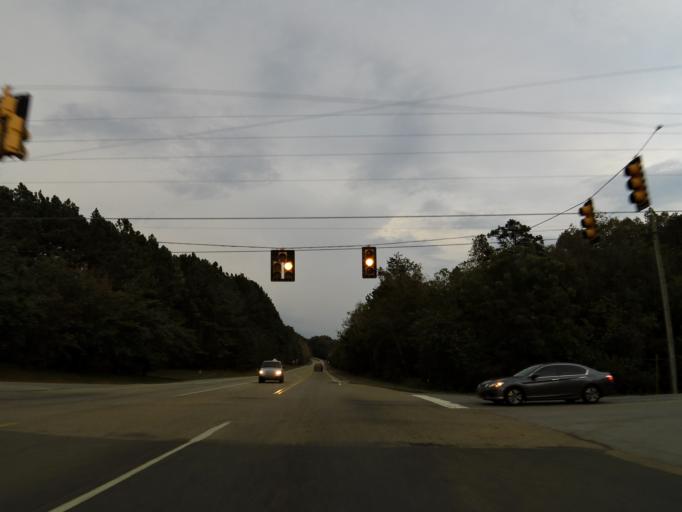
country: US
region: Tennessee
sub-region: Loudon County
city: Loudon
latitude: 35.6929
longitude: -84.2604
